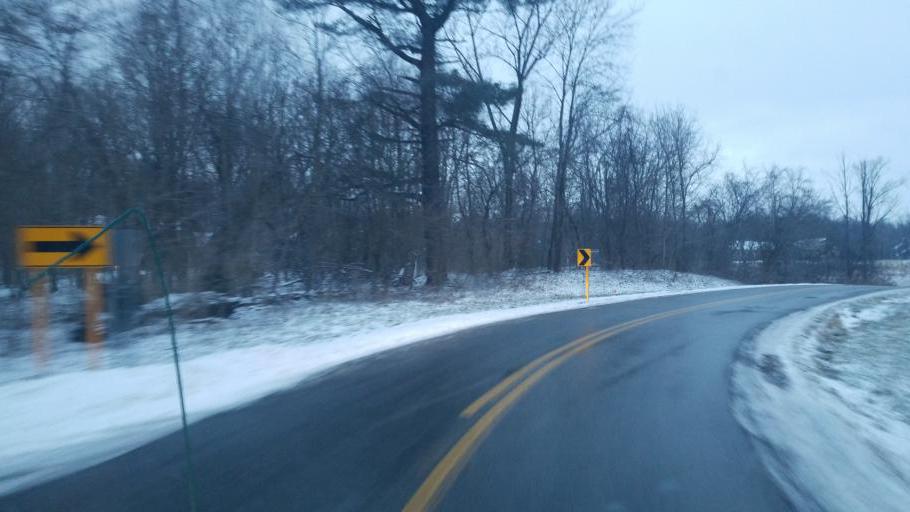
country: US
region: Ohio
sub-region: Delaware County
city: Sunbury
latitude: 40.2056
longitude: -82.8527
